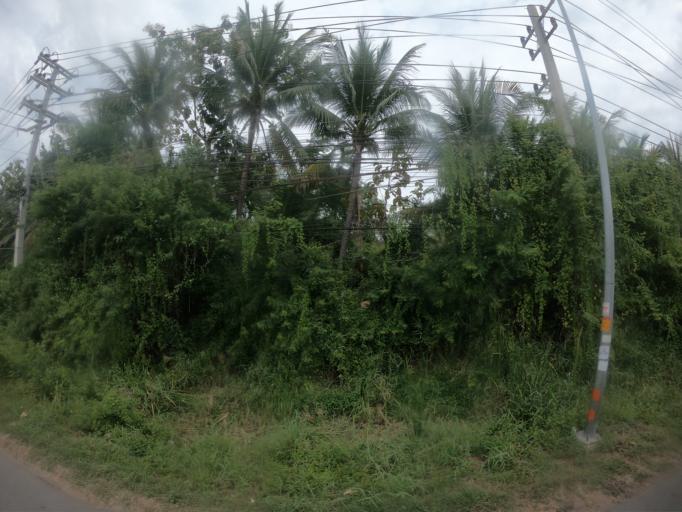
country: TH
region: Maha Sarakham
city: Maha Sarakham
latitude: 16.1774
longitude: 103.3133
